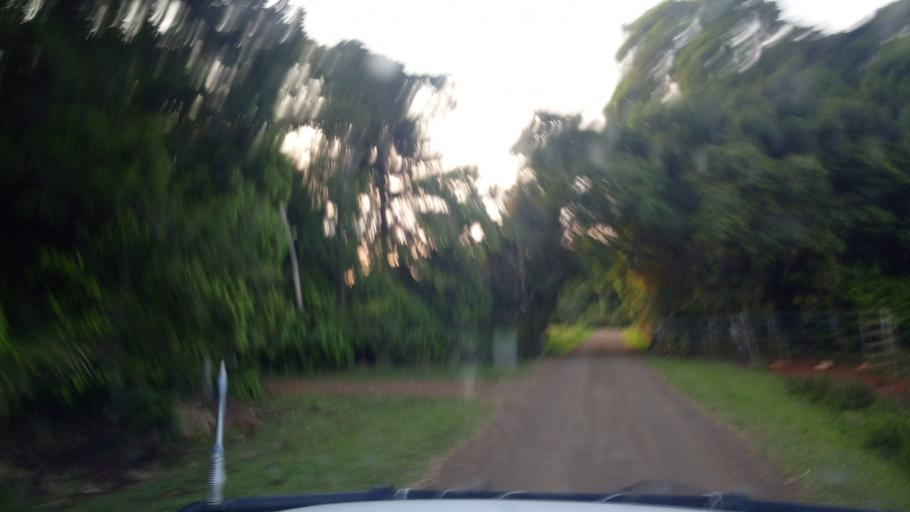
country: AU
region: Queensland
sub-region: Tablelands
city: Atherton
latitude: -17.3653
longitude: 145.7504
